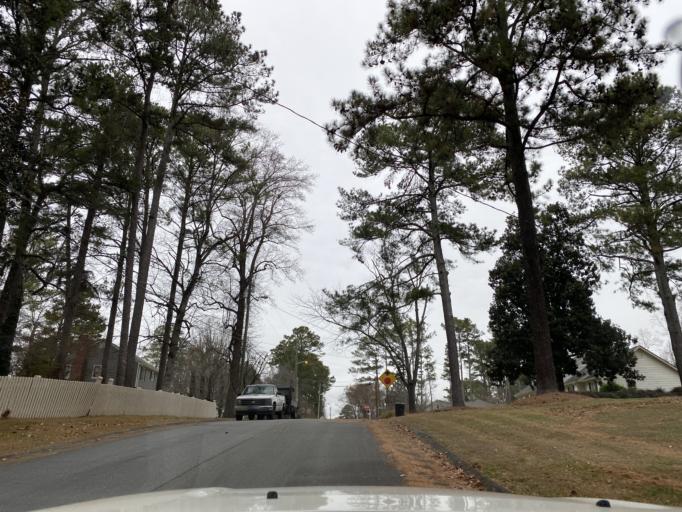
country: US
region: Georgia
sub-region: Cobb County
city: Fair Oaks
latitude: 33.9172
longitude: -84.5697
